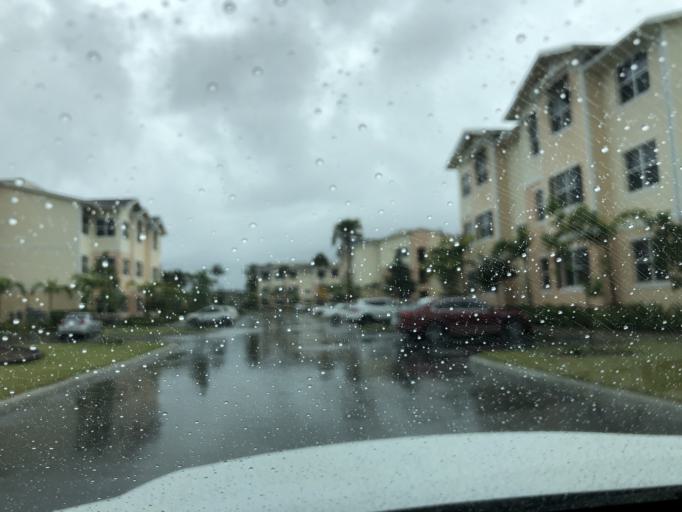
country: US
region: Florida
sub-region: Palm Beach County
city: Plantation Mobile Home Park
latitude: 26.6978
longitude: -80.1272
